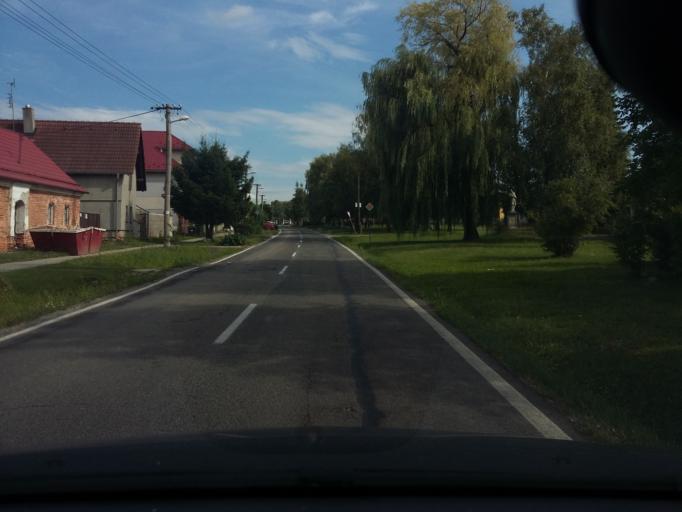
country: SK
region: Trnavsky
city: Gbely
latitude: 48.5808
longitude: 17.1810
